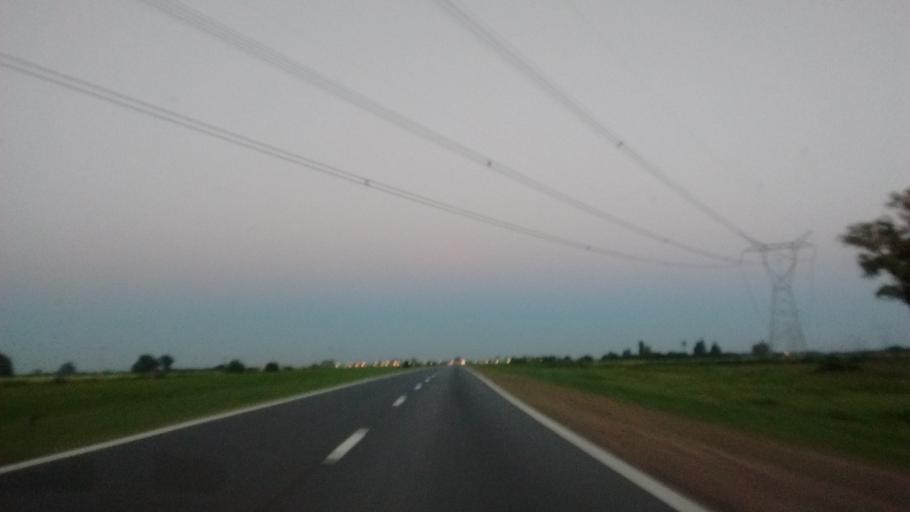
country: AR
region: Santa Fe
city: Roldan
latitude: -32.9235
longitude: -60.9151
